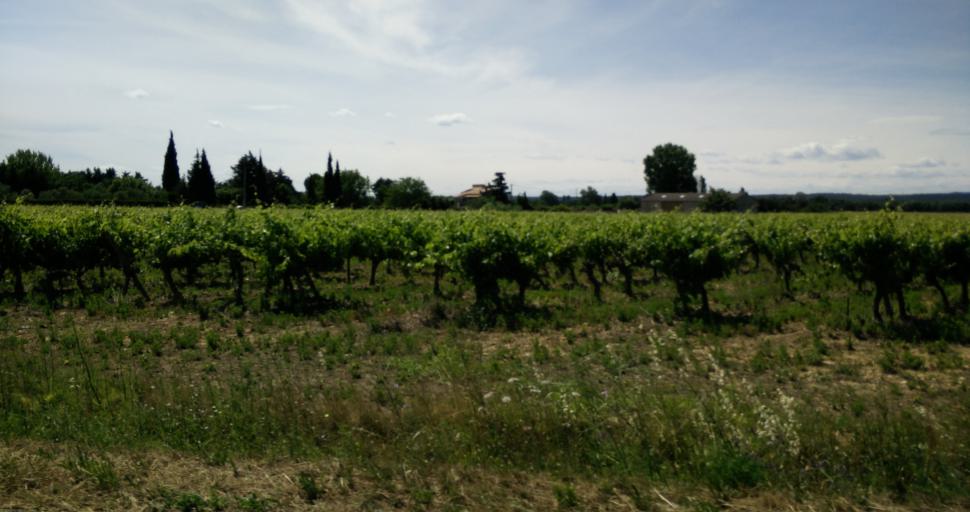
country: FR
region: Languedoc-Roussillon
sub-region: Departement du Gard
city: Aubord
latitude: 43.7551
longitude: 4.3094
